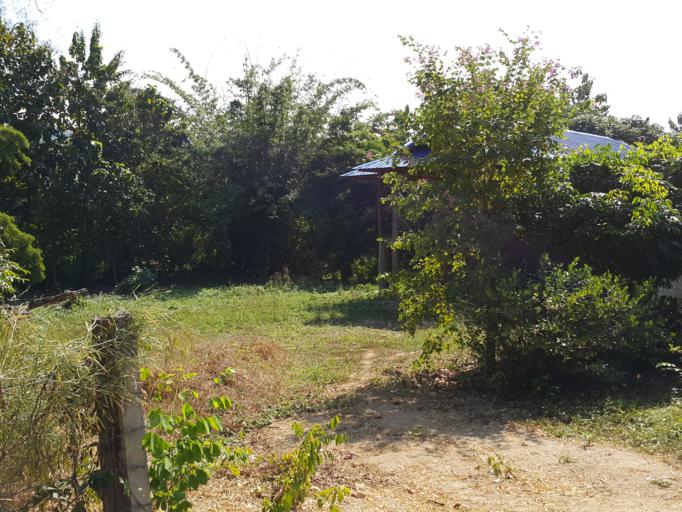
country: TH
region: Sukhothai
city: Thung Saliam
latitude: 17.3323
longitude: 99.4592
